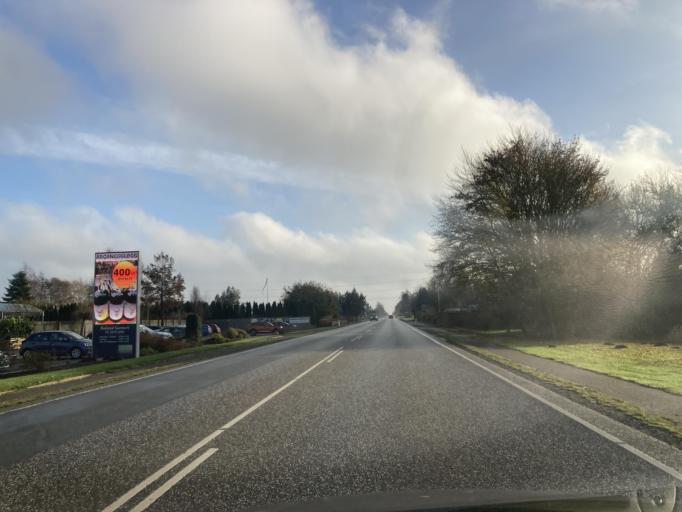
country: DK
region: Zealand
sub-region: Guldborgsund Kommune
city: Sakskobing
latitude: 54.7868
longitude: 11.6879
